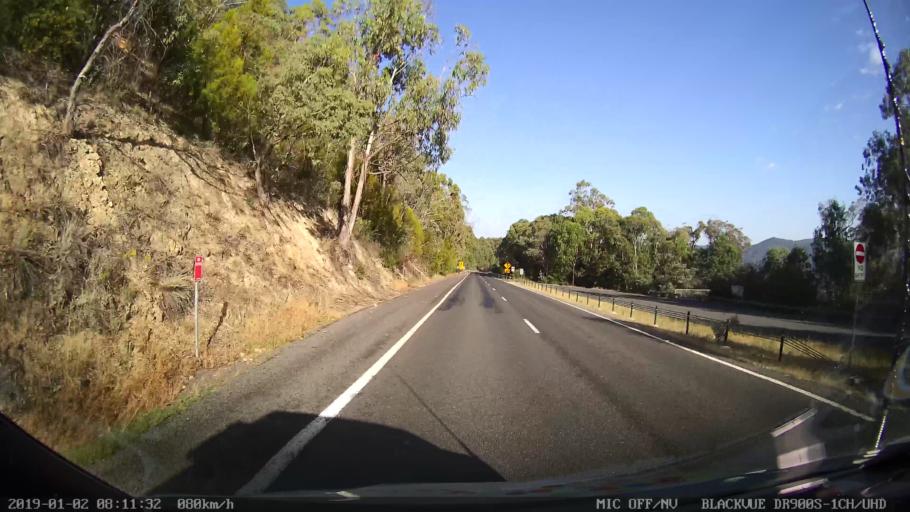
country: AU
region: New South Wales
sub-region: Tumut Shire
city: Tumut
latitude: -35.5953
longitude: 148.3567
